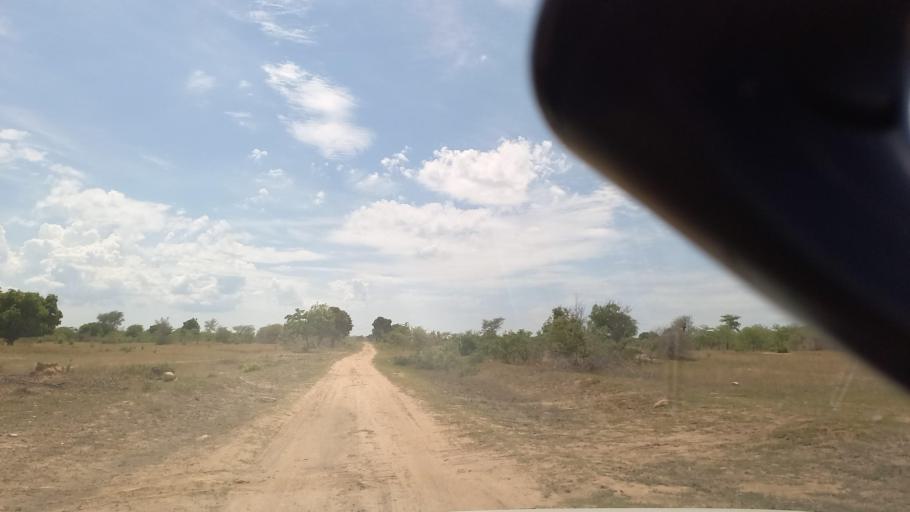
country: ZM
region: Southern
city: Mazabuka
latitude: -16.1415
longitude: 27.7658
